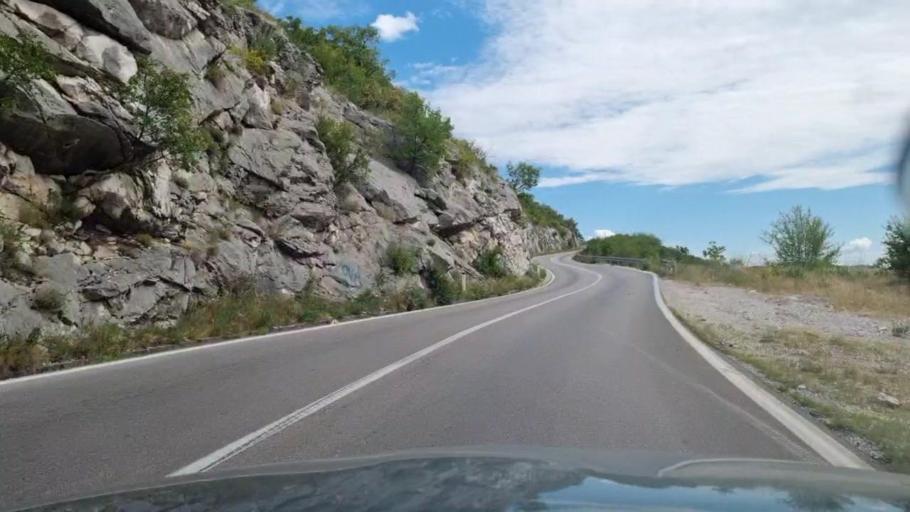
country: BA
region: Federation of Bosnia and Herzegovina
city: Blagaj
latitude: 43.2703
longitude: 17.9316
